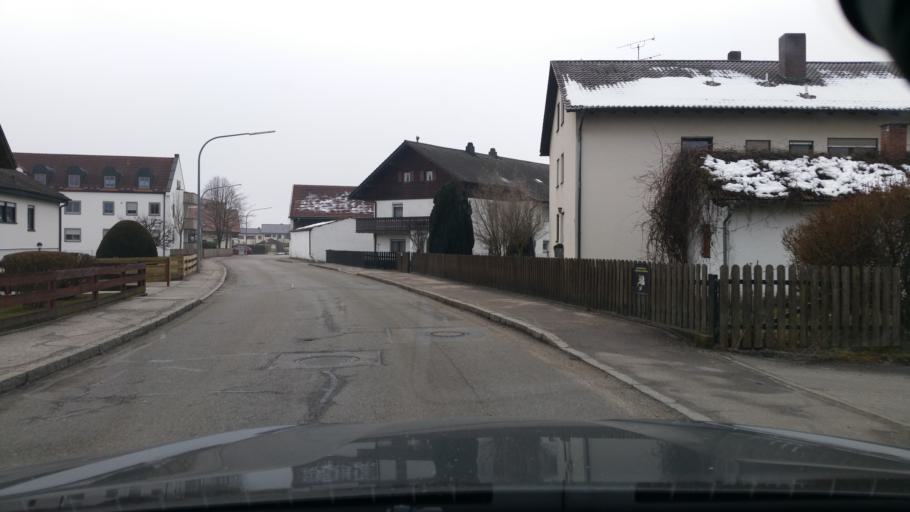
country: DE
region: Bavaria
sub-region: Lower Bavaria
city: Tiefenbach
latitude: 48.5555
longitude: 12.1035
